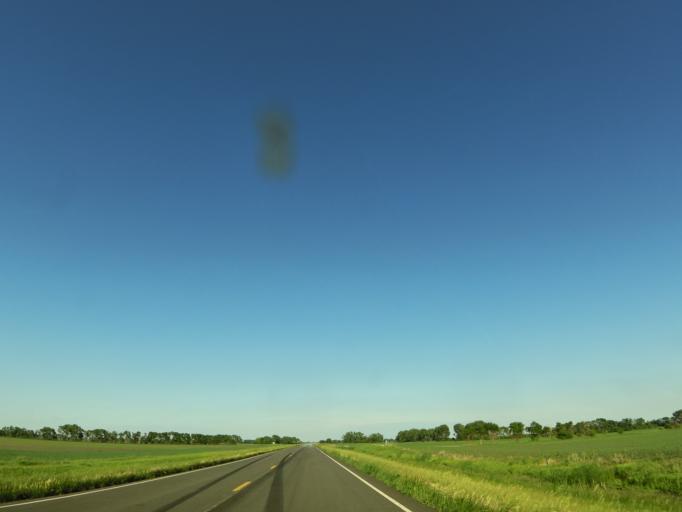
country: US
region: North Dakota
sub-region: Grand Forks County
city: Grand Forks Air Force Base
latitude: 48.1358
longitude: -97.2316
